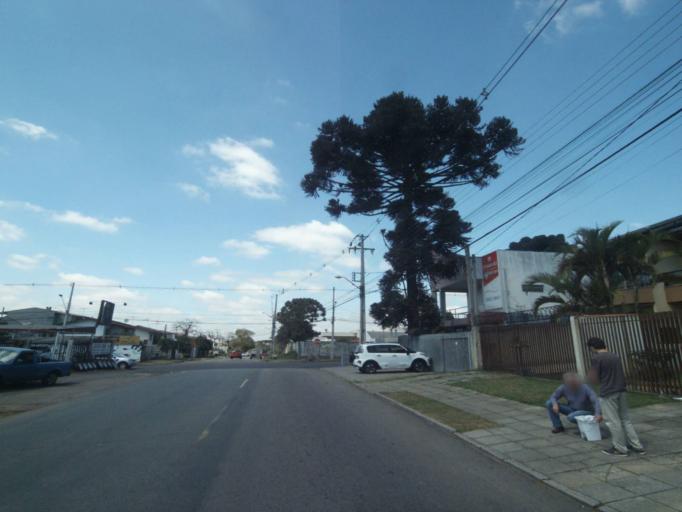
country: BR
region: Parana
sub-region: Sao Jose Dos Pinhais
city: Sao Jose dos Pinhais
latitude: -25.5202
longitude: -49.2367
